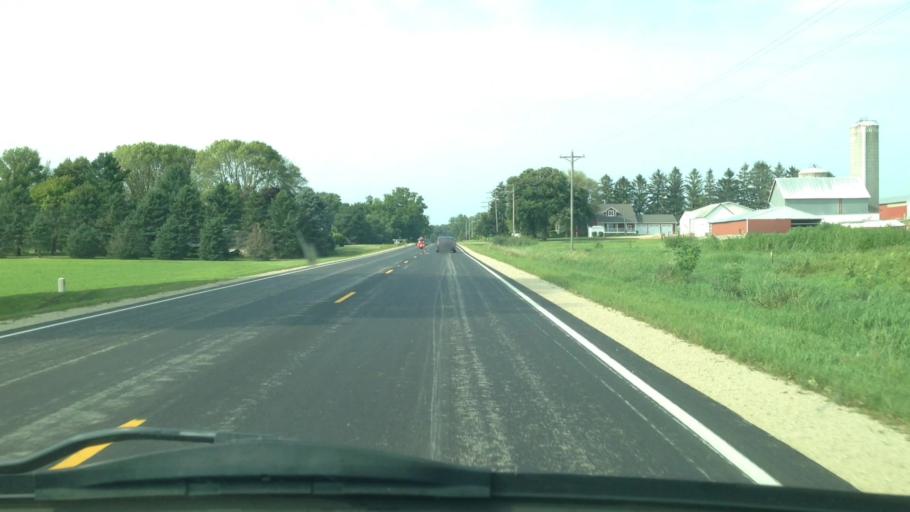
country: US
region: Minnesota
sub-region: Winona County
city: Lewiston
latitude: 43.9572
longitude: -91.9543
